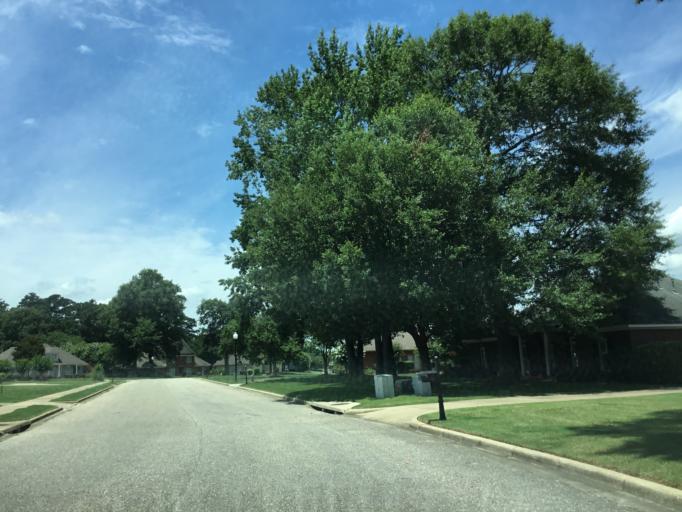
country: US
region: Alabama
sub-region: Montgomery County
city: Pike Road
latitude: 32.3791
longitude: -86.1354
